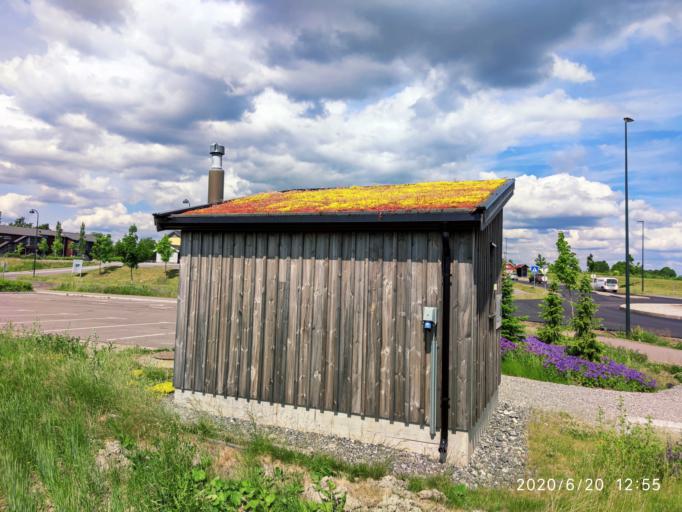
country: NO
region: Akershus
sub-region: Gjerdrum
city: Ask
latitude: 60.0643
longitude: 11.0410
